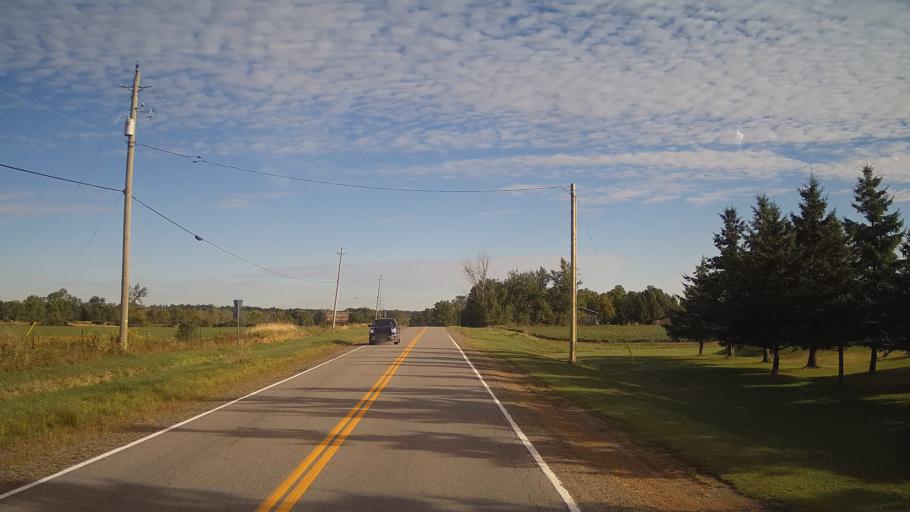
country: CA
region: Ontario
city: Gananoque
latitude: 44.3795
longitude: -76.1384
